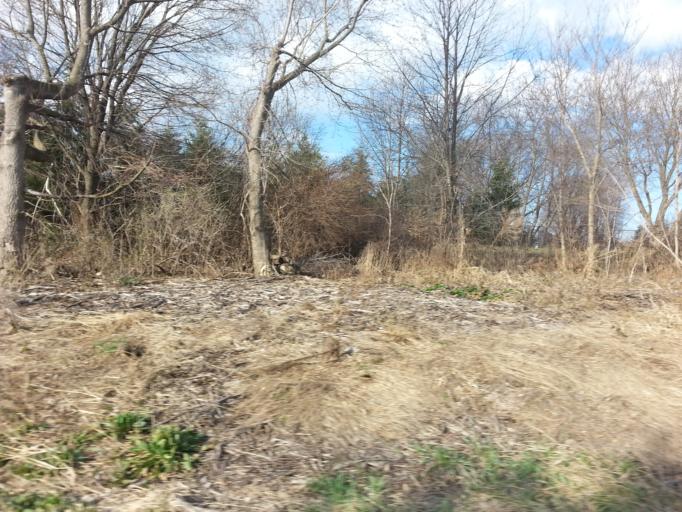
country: US
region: Minnesota
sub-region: Dakota County
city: Hastings
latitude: 44.7685
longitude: -92.8402
